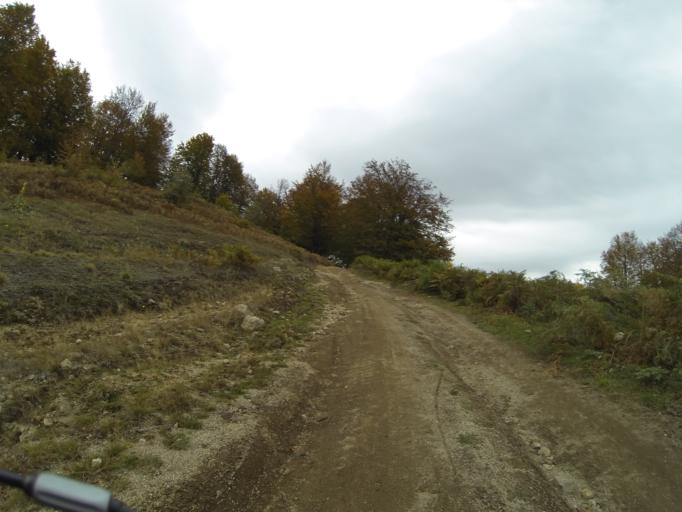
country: RO
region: Gorj
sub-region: Comuna Tismana
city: Sohodol
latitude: 45.1282
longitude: 22.8653
